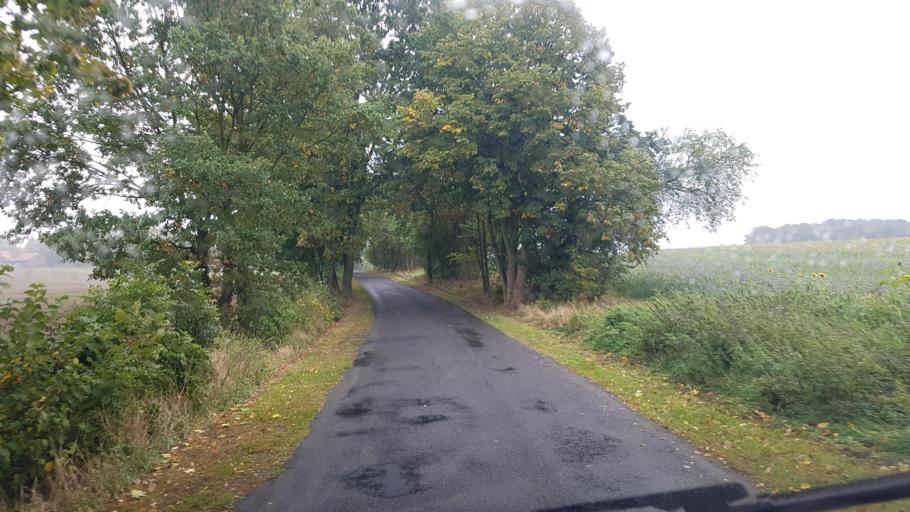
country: DE
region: Brandenburg
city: Furstenwalde
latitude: 52.4005
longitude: 14.0579
